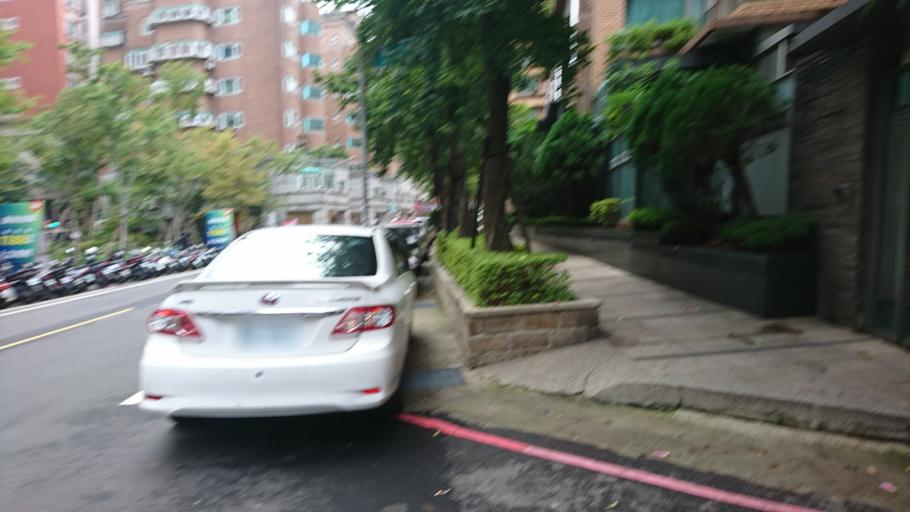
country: TW
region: Taiwan
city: Taoyuan City
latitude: 25.0569
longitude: 121.2965
